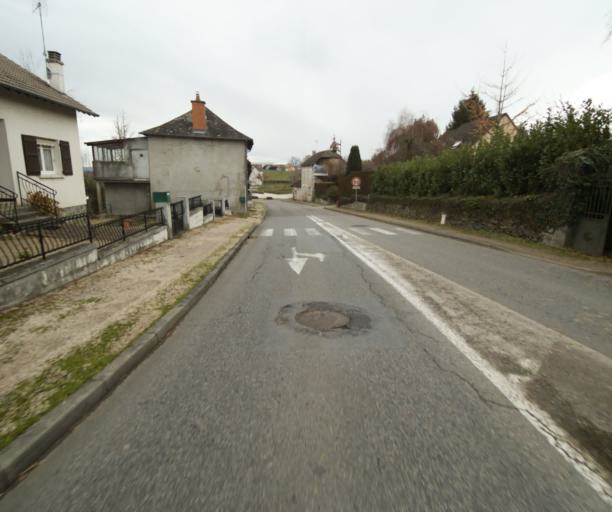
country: FR
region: Limousin
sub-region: Departement de la Correze
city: Chameyrat
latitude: 45.2656
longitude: 1.7233
